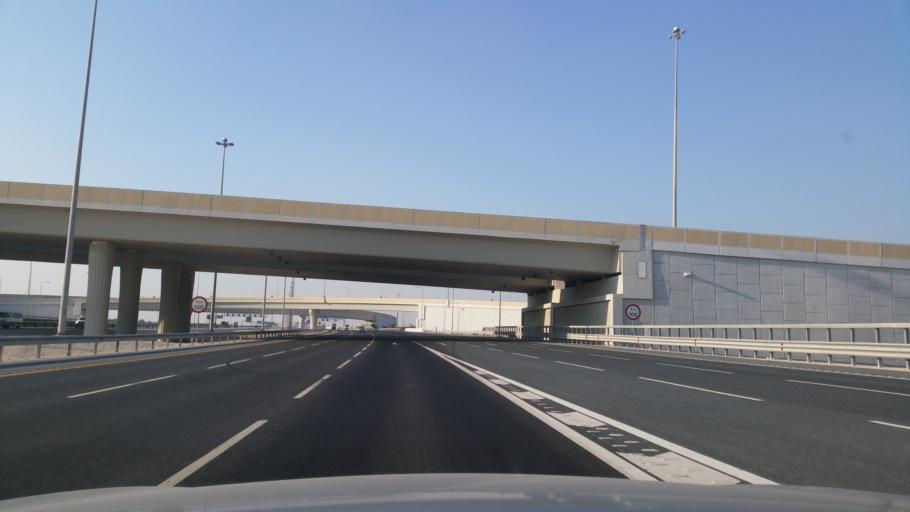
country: QA
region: Al Wakrah
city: Al Wakrah
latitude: 25.1314
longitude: 51.5866
